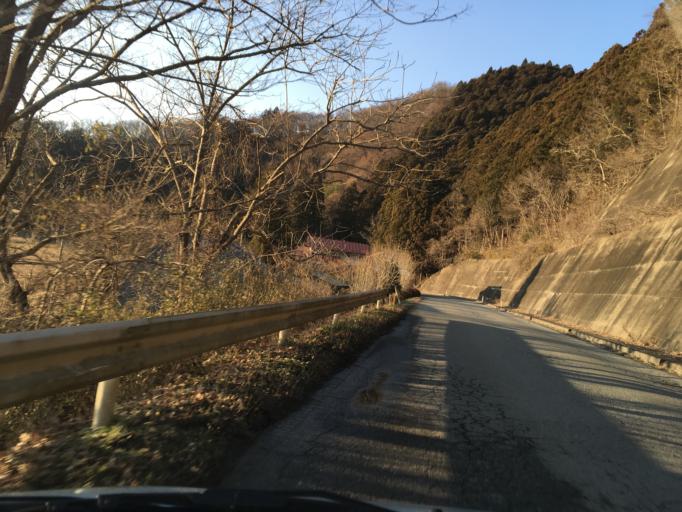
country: JP
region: Iwate
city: Ichinoseki
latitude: 38.8022
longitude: 141.2392
